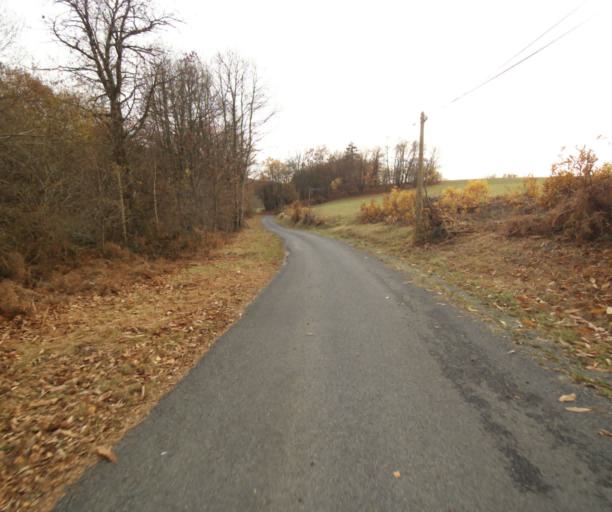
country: FR
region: Limousin
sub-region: Departement de la Correze
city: Sainte-Fortunade
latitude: 45.1872
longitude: 1.7579
